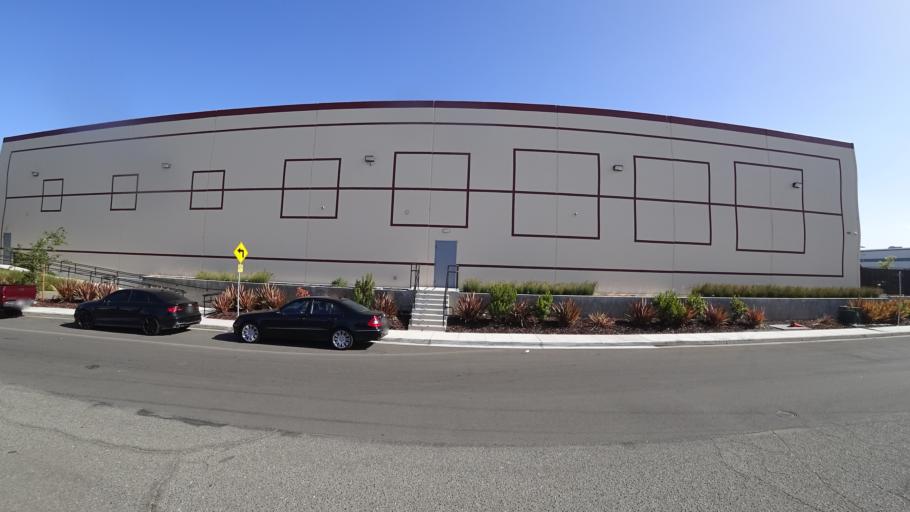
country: US
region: California
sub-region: Alameda County
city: San Lorenzo
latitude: 37.6444
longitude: -122.1340
